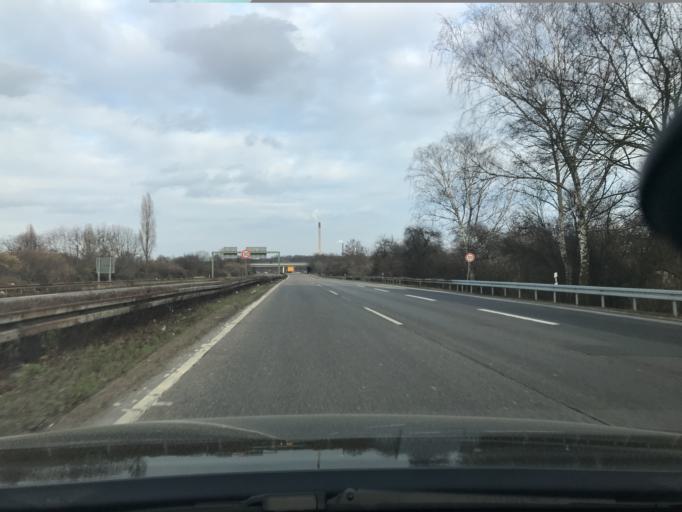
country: DE
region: North Rhine-Westphalia
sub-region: Regierungsbezirk Dusseldorf
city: Krefeld
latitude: 51.3713
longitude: 6.6300
